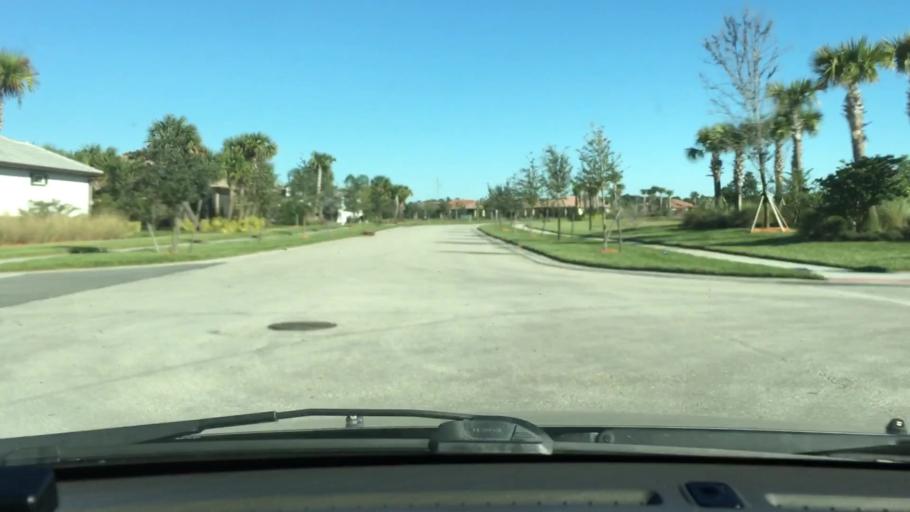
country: US
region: Florida
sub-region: Indian River County
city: Gifford
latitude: 27.6876
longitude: -80.4320
